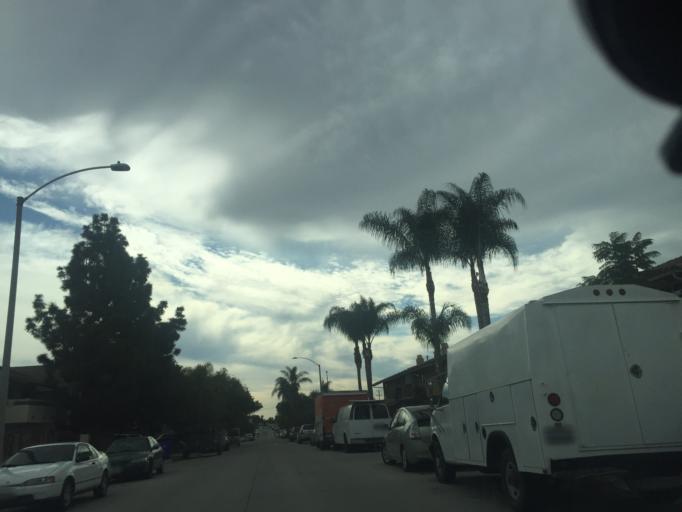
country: US
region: California
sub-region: San Diego County
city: Lemon Grove
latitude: 32.7541
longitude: -117.0912
